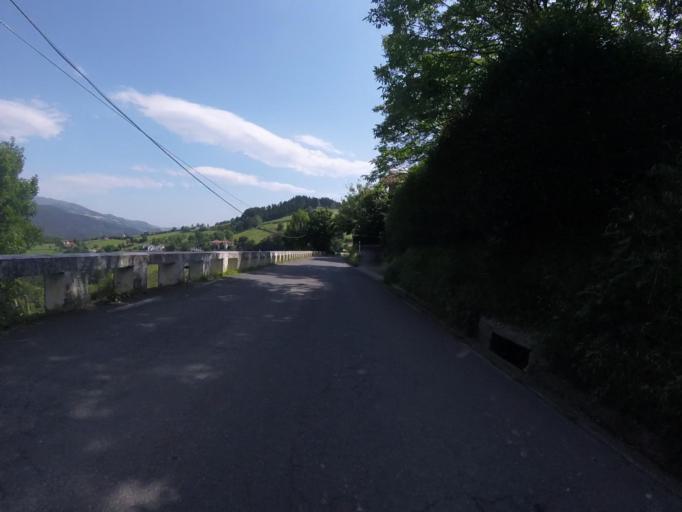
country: ES
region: Basque Country
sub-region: Provincia de Guipuzcoa
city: Orendain
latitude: 43.0811
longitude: -2.1090
